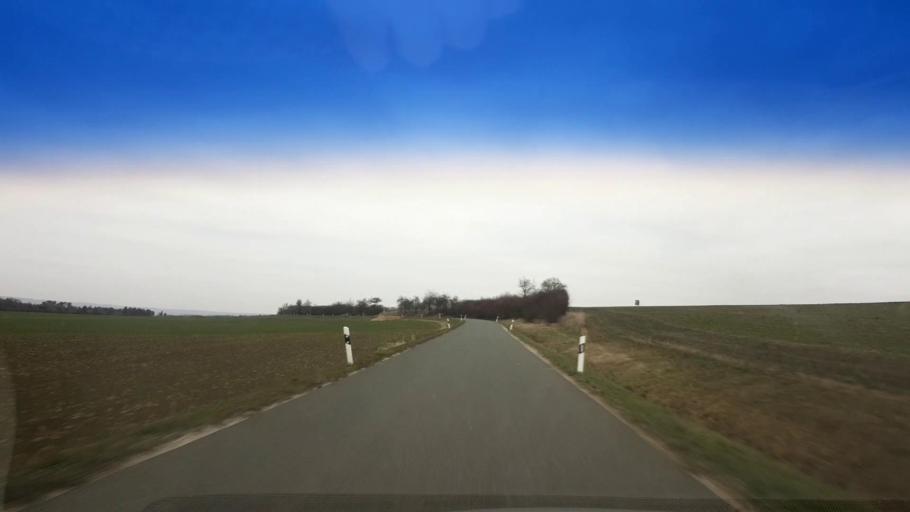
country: DE
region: Bavaria
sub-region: Upper Franconia
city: Hallerndorf
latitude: 49.7676
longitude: 10.9279
